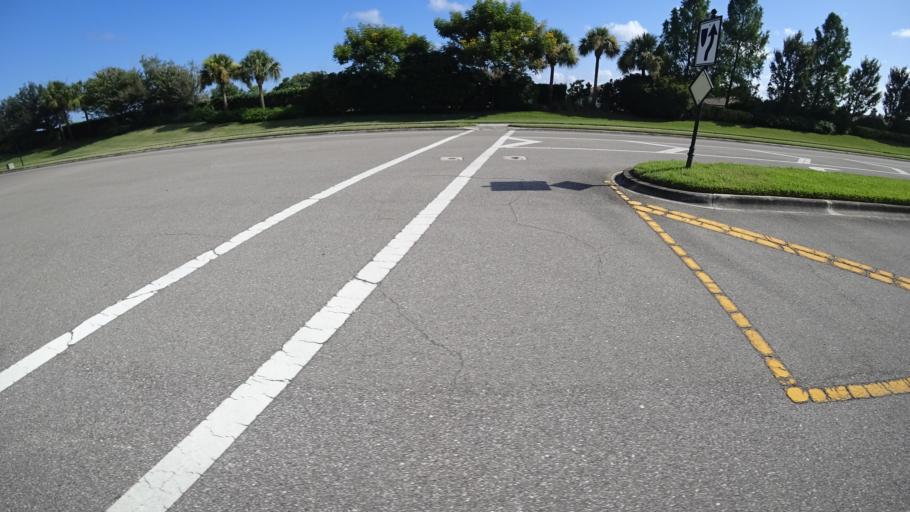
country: US
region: Florida
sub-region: Manatee County
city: Ellenton
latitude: 27.5038
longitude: -82.4701
